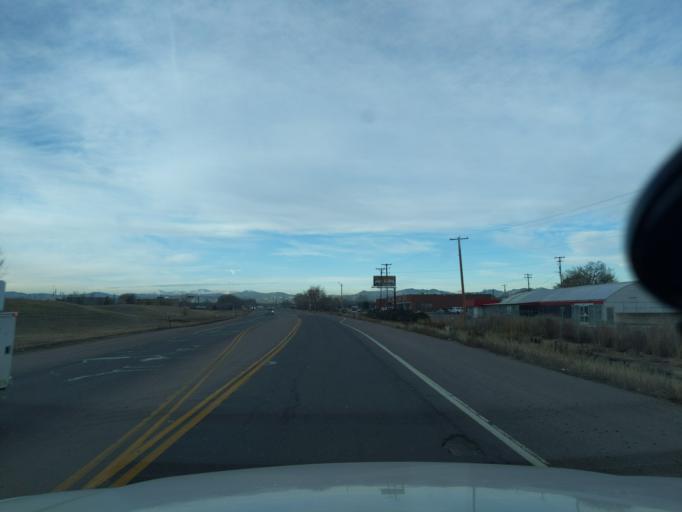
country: US
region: Colorado
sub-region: Adams County
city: Welby
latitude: 39.8305
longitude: -104.9526
